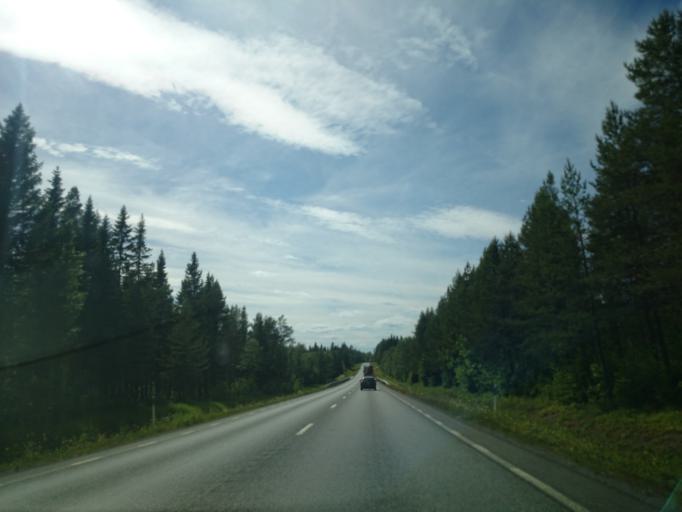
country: SE
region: Jaemtland
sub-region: Krokoms Kommun
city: Krokom
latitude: 63.3228
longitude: 14.2678
